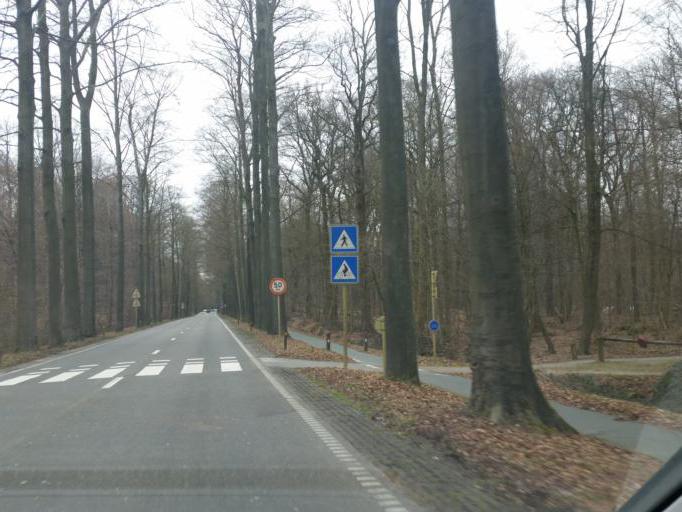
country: BE
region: Flanders
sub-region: Provincie Vlaams-Brabant
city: Linkebeek
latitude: 50.7944
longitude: 4.3838
